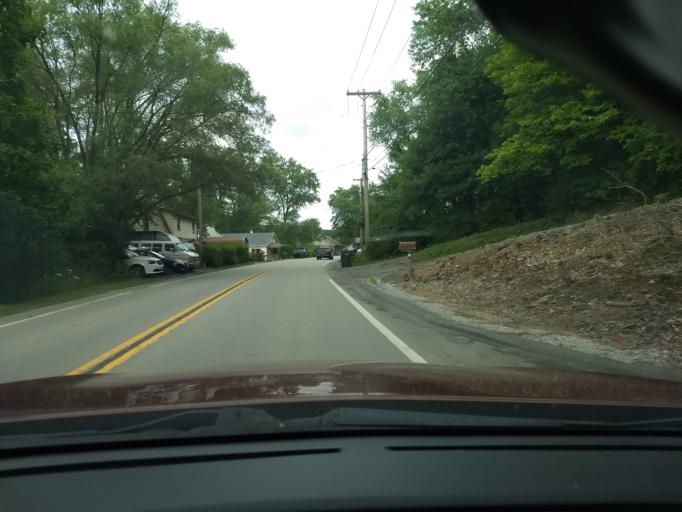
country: US
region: Pennsylvania
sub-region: Allegheny County
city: Bradford Woods
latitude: 40.6540
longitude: -80.0759
